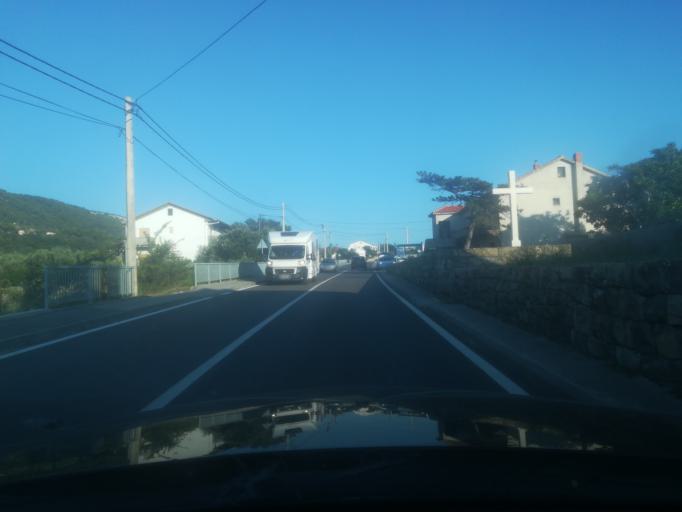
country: HR
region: Primorsko-Goranska
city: Banjol
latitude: 44.7707
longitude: 14.7633
